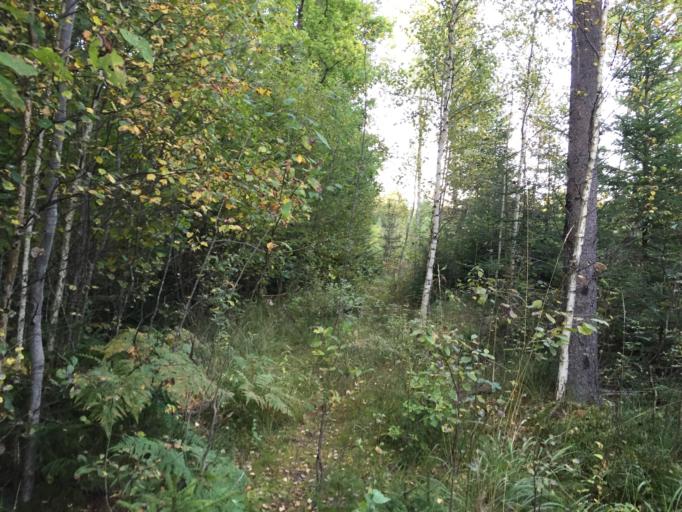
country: LV
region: Seja
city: Loja
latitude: 57.1294
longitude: 24.6180
